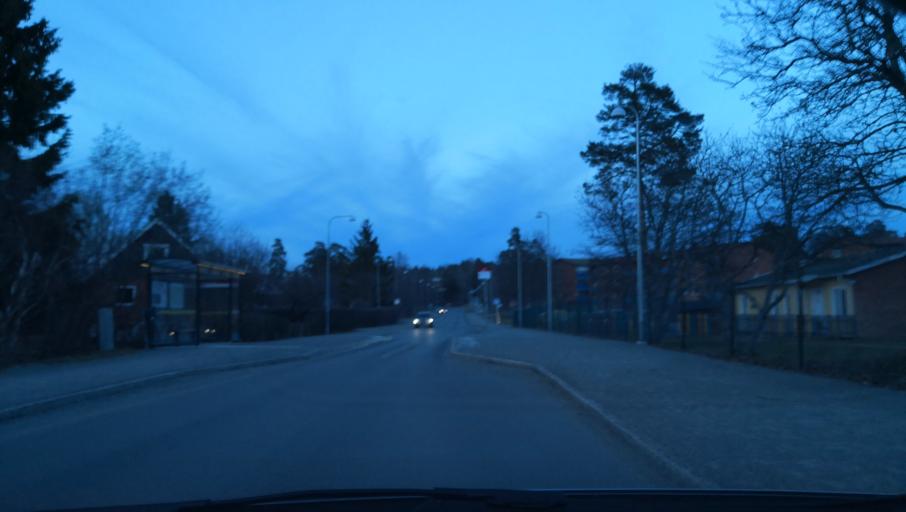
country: SE
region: Stockholm
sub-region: Varmdo Kommun
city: Gustavsberg
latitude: 59.3343
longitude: 18.3914
